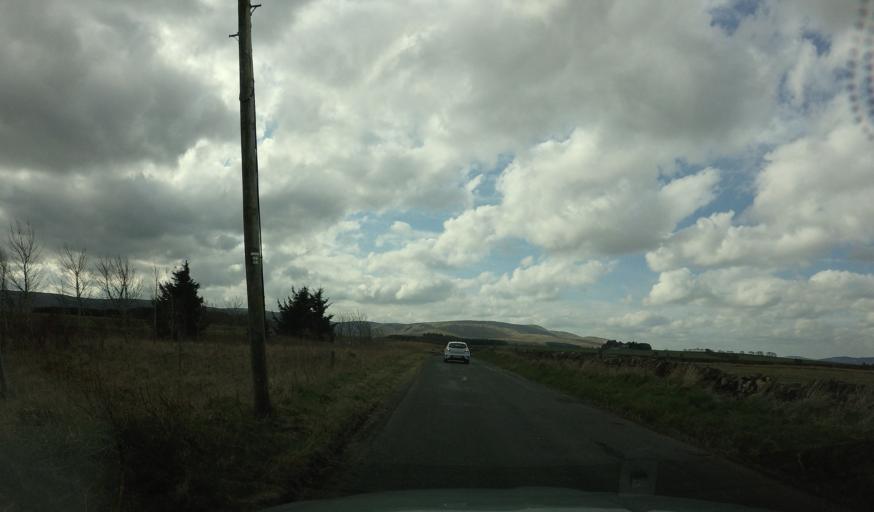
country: GB
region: Scotland
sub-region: Midlothian
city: Bonnyrigg
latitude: 55.7861
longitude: -3.1313
